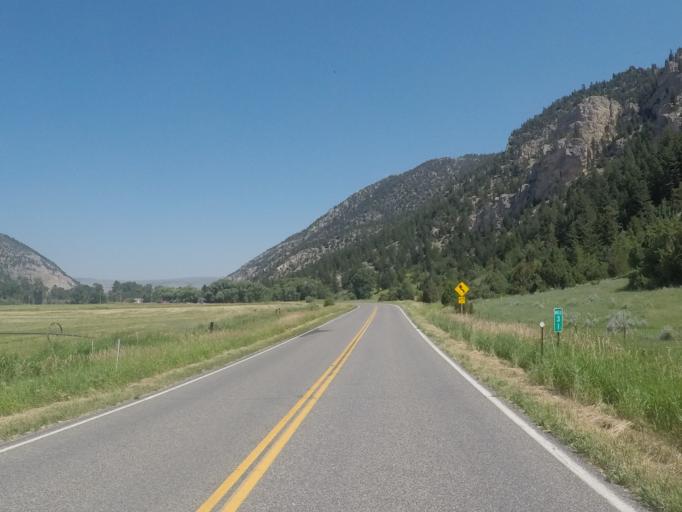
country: US
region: Montana
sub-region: Park County
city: Livingston
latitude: 45.5920
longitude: -110.5612
